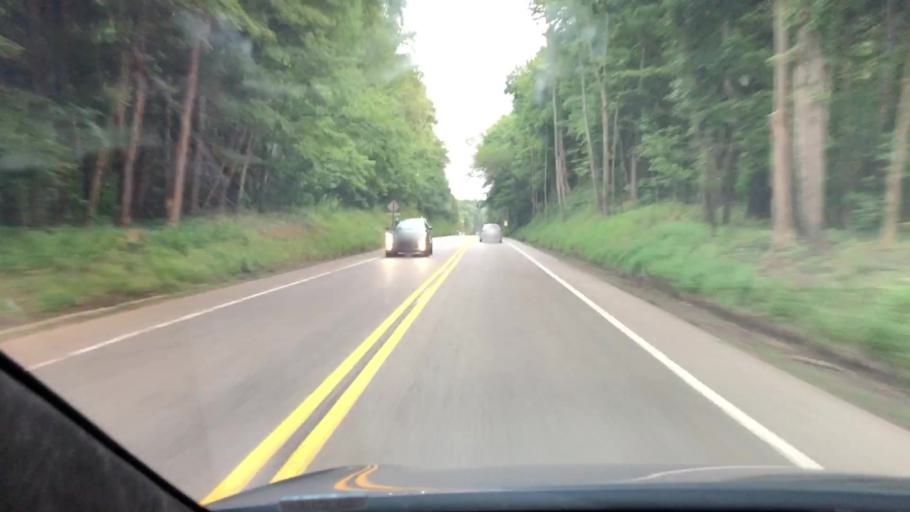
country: US
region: Pennsylvania
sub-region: Butler County
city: Slippery Rock
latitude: 41.0162
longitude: -80.0050
